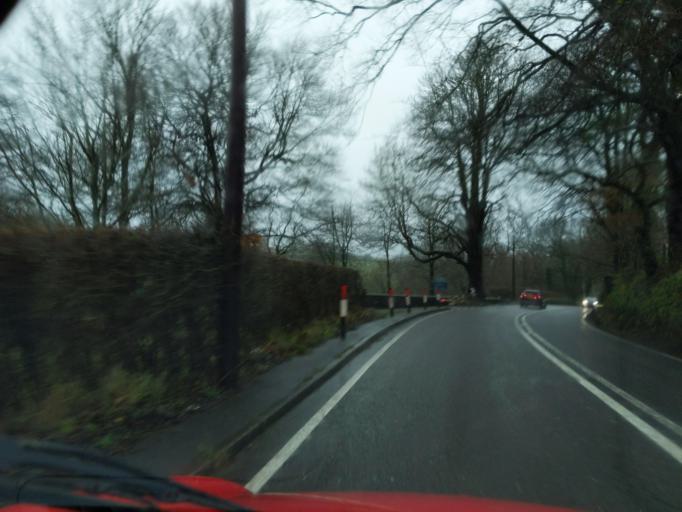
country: GB
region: England
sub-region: Cornwall
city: South Hill
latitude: 50.5819
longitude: -4.3324
